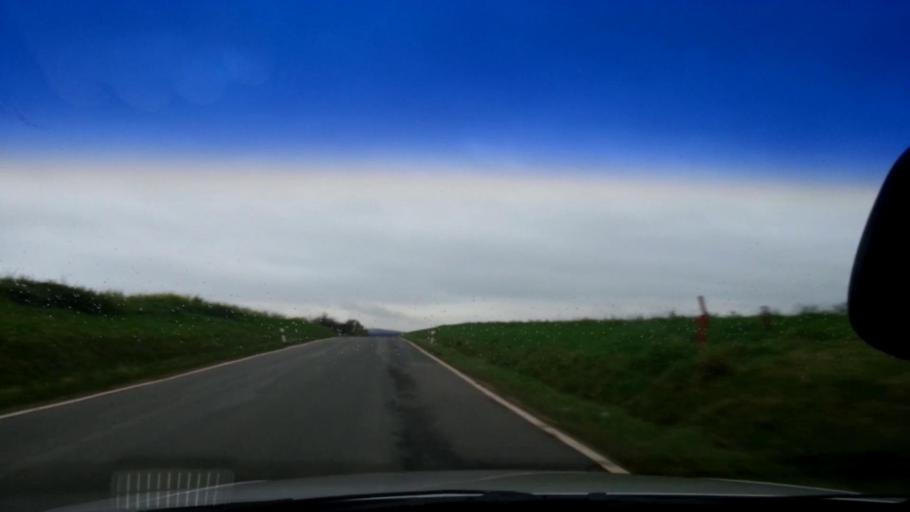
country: DE
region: Bavaria
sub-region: Upper Franconia
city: Schesslitz
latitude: 49.9572
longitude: 11.0185
